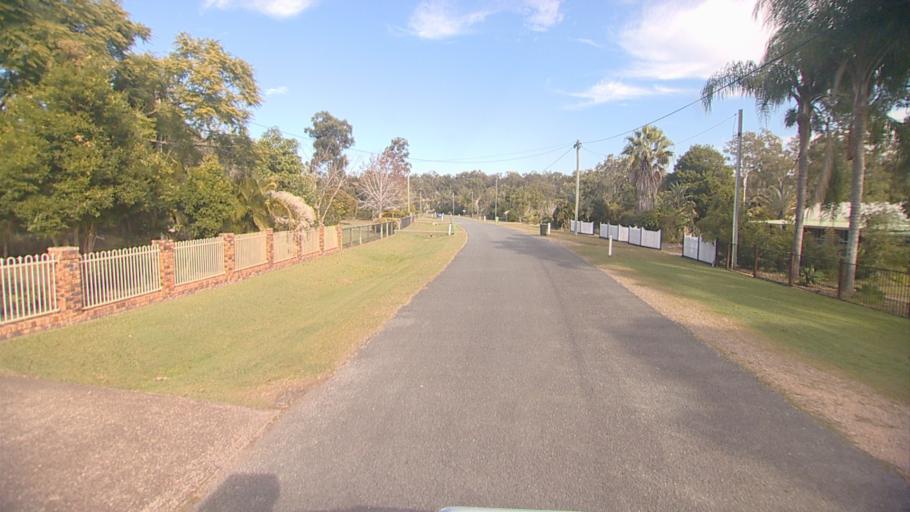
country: AU
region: Queensland
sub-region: Logan
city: Park Ridge South
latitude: -27.7385
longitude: 153.0403
